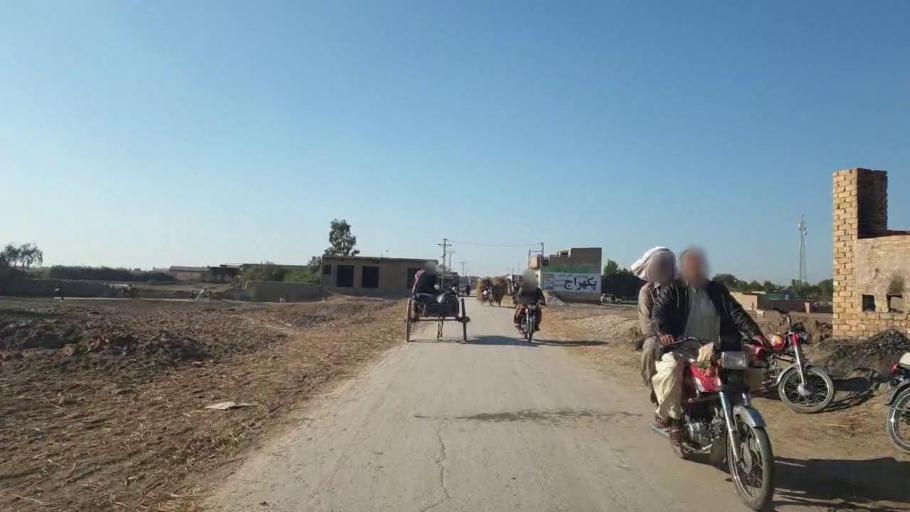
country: PK
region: Sindh
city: New Badah
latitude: 27.3250
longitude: 68.0320
